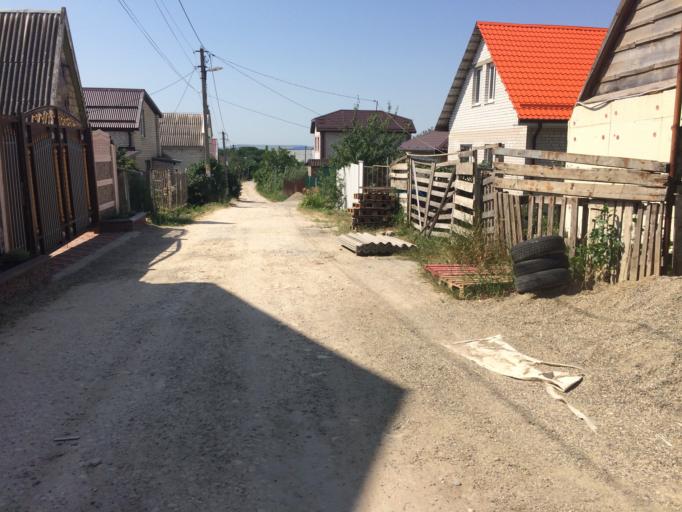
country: RU
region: Stavropol'skiy
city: Tatarka
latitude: 44.9833
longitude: 41.9414
